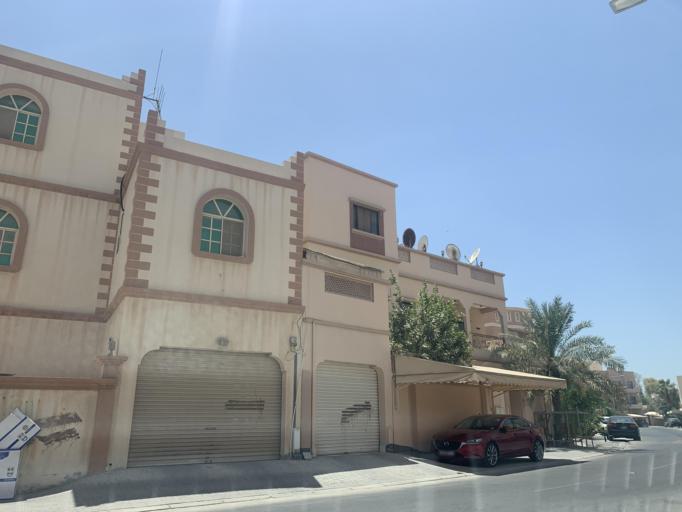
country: BH
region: Manama
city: Jidd Hafs
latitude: 26.2212
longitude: 50.5133
